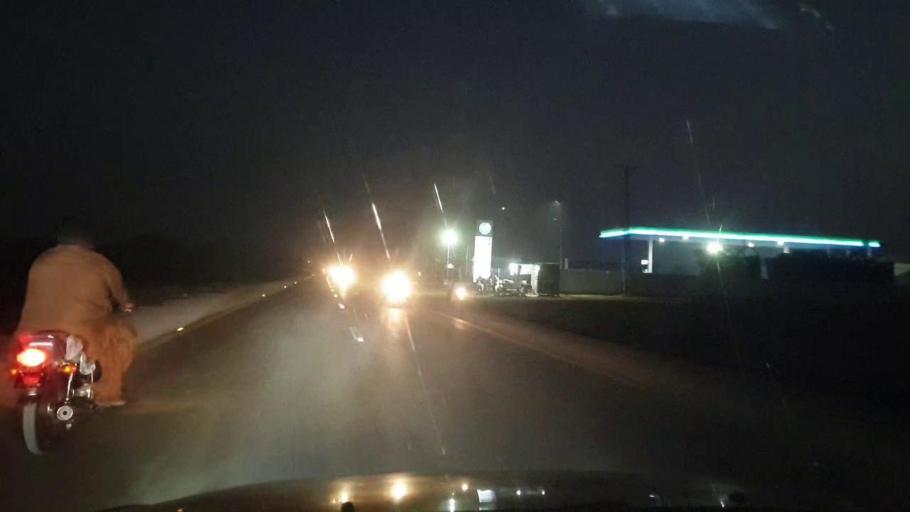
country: PK
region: Sindh
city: Chambar
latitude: 25.3097
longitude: 68.8069
